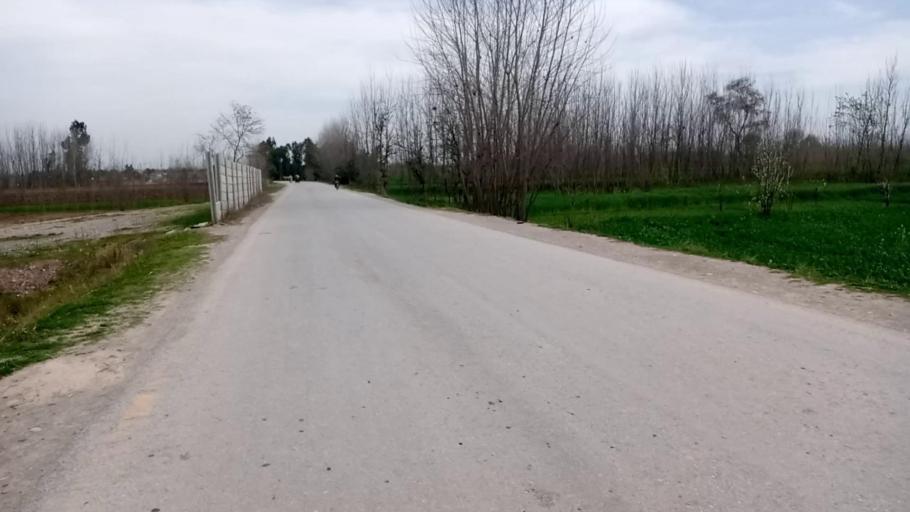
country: PK
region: Khyber Pakhtunkhwa
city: Charsadda
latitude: 34.0622
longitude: 71.6967
